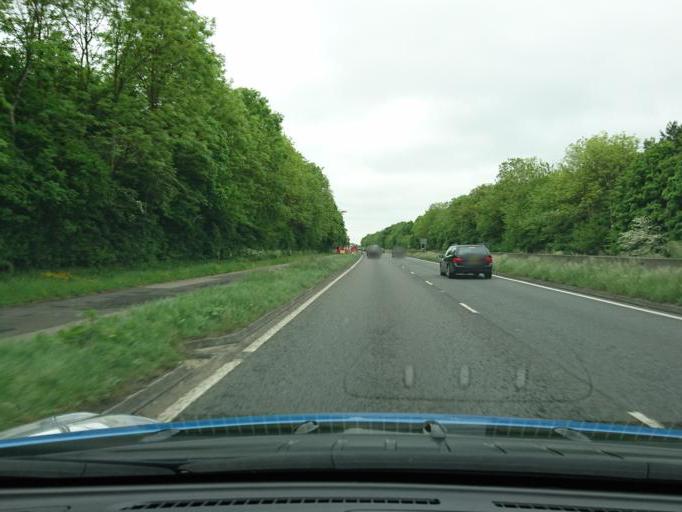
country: GB
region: England
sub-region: Oxfordshire
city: Cowley
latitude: 51.7456
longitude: -1.1956
